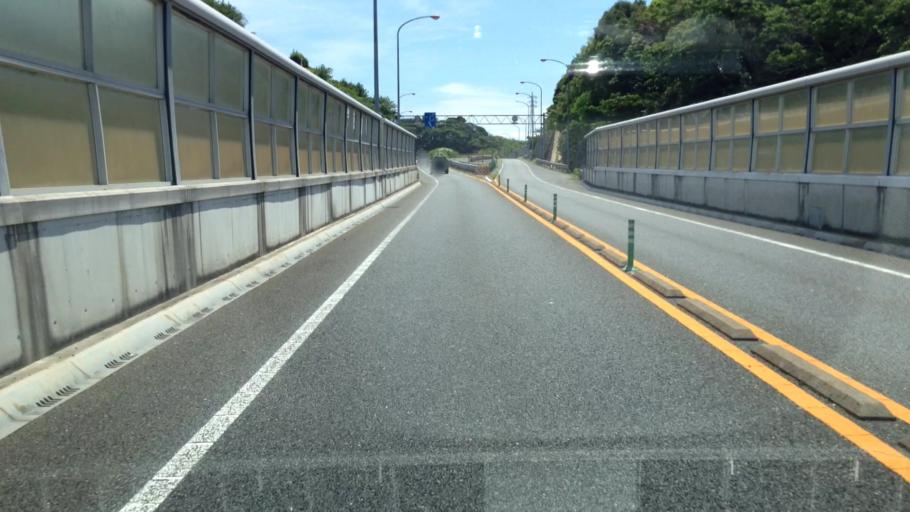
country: JP
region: Kanagawa
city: Yokosuka
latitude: 35.2162
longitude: 139.6375
